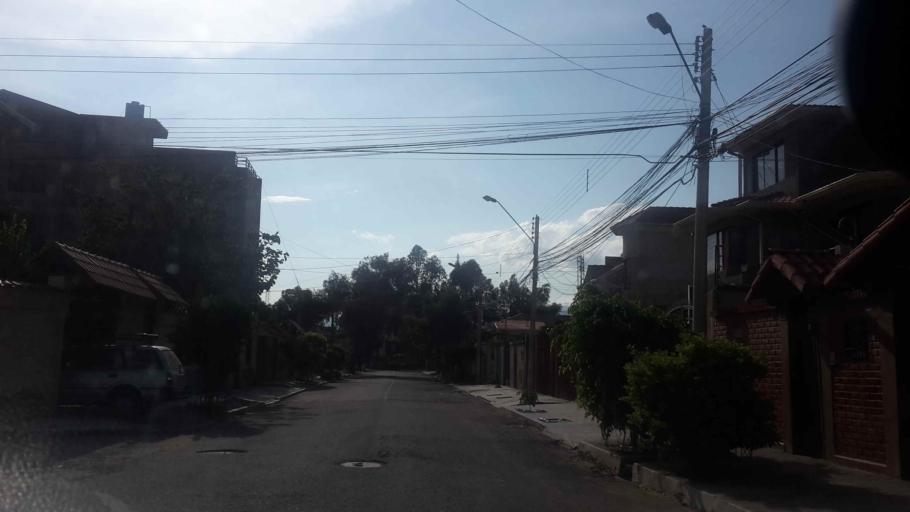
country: BO
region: Cochabamba
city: Cochabamba
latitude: -17.3791
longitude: -66.1947
